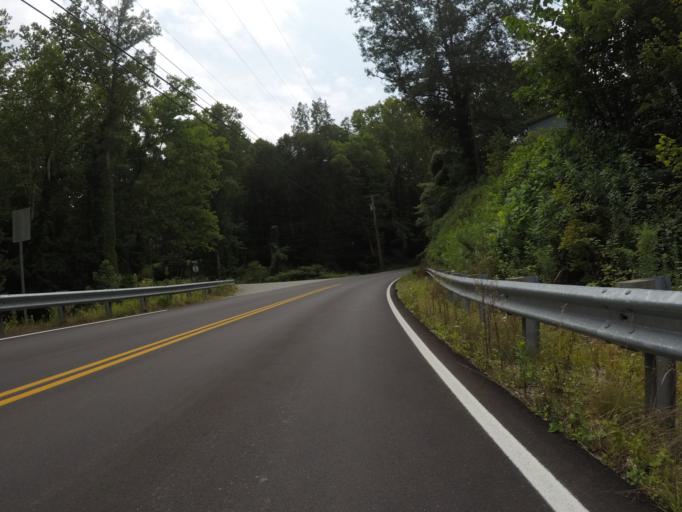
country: US
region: Kentucky
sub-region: Boyd County
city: Catlettsburg
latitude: 38.4364
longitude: -82.6276
